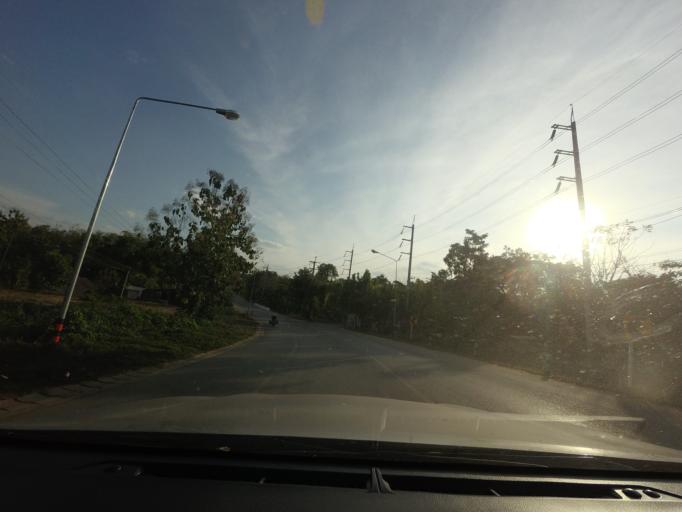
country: TH
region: Mae Hong Son
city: Mae Hi
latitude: 19.3453
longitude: 98.4328
